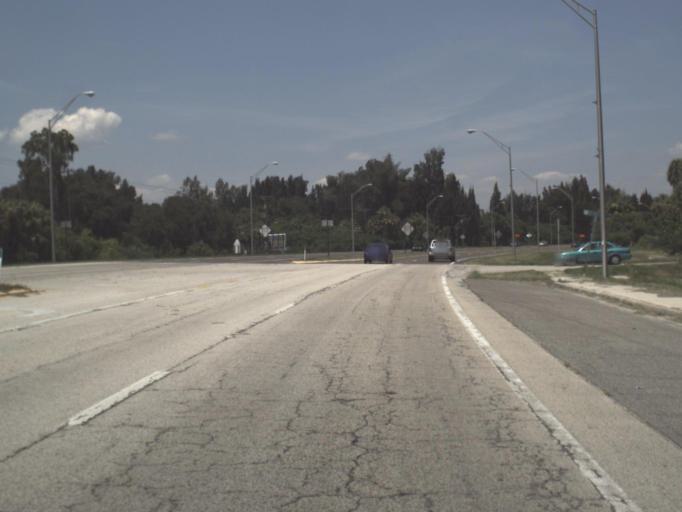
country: US
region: Florida
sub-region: Hillsborough County
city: Ruskin
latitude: 27.7311
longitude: -82.4336
